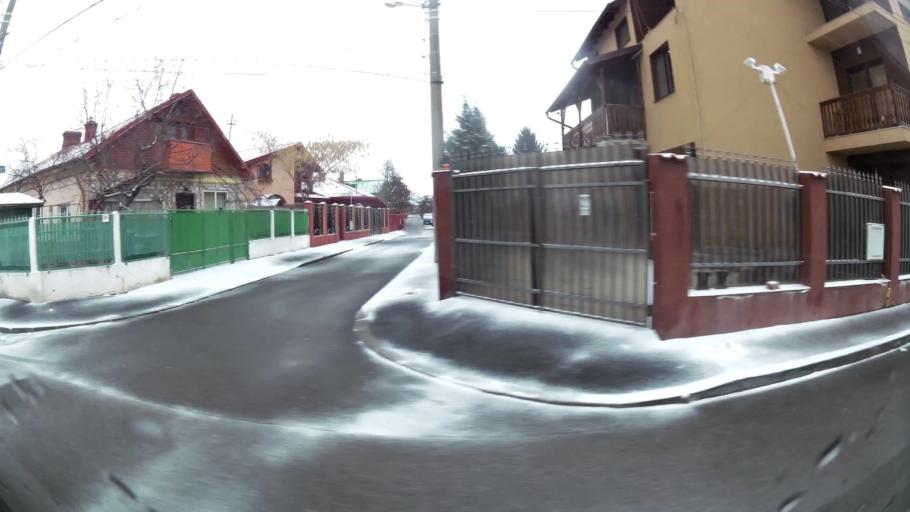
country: RO
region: Prahova
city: Ploiesti
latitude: 44.9263
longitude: 26.0205
